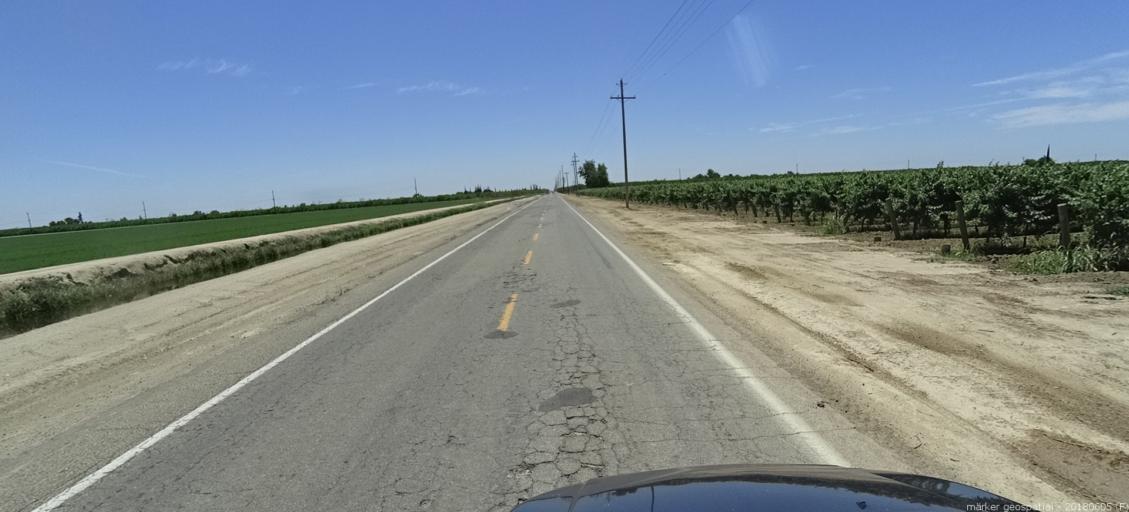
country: US
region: California
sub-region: Madera County
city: Chowchilla
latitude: 37.1307
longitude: -120.3109
